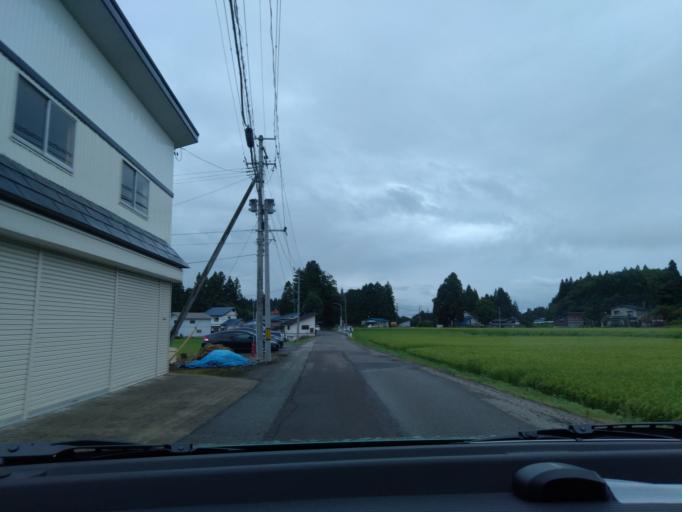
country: JP
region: Akita
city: Yokotemachi
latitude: 39.4191
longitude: 140.5936
